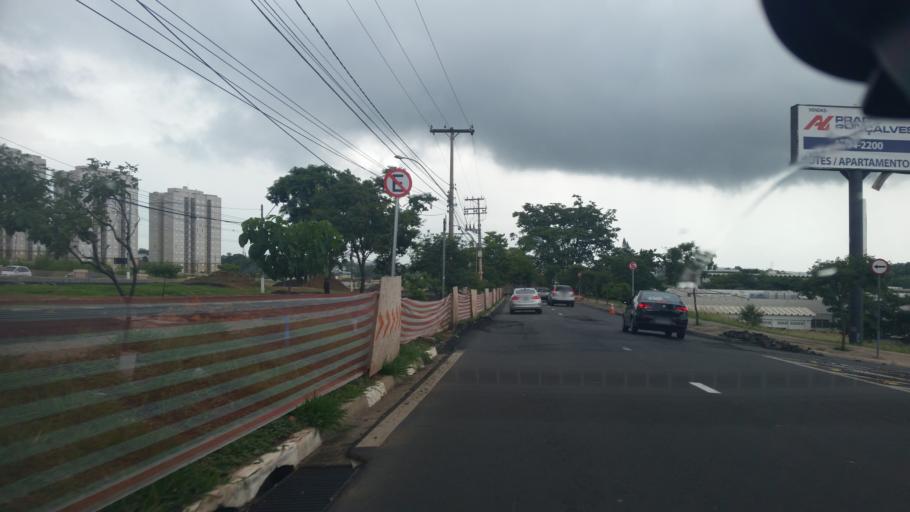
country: BR
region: Sao Paulo
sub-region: Campinas
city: Campinas
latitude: -22.9216
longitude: -47.1175
